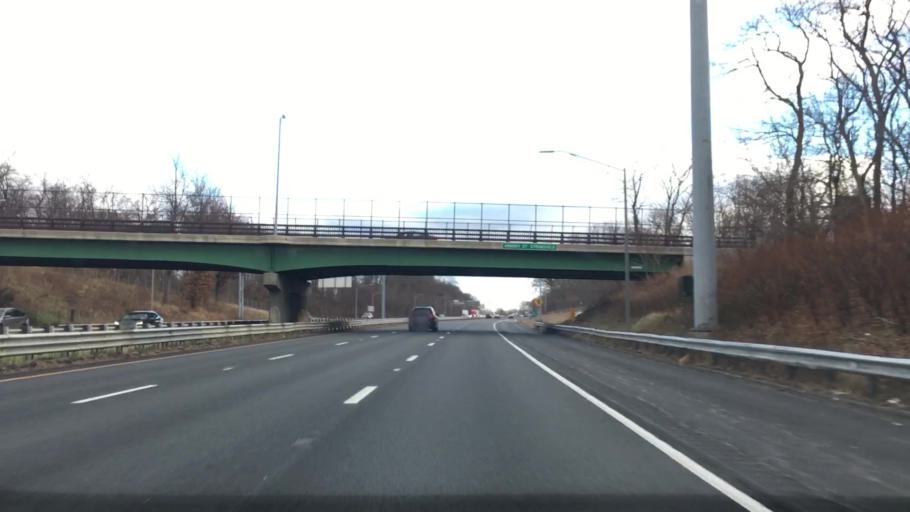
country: US
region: Massachusetts
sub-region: Hampden County
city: Springfield
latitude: 42.1182
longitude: -72.5842
